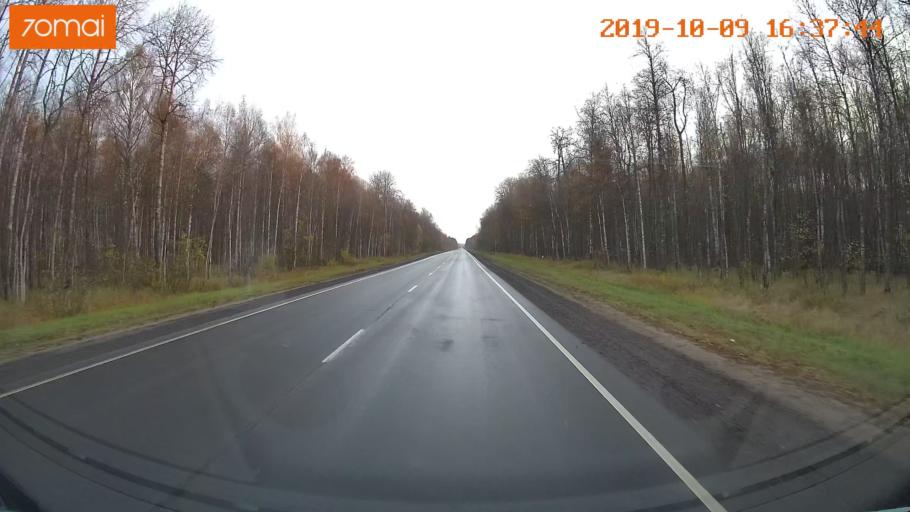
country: RU
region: Kostroma
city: Volgorechensk
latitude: 57.5224
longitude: 41.0284
